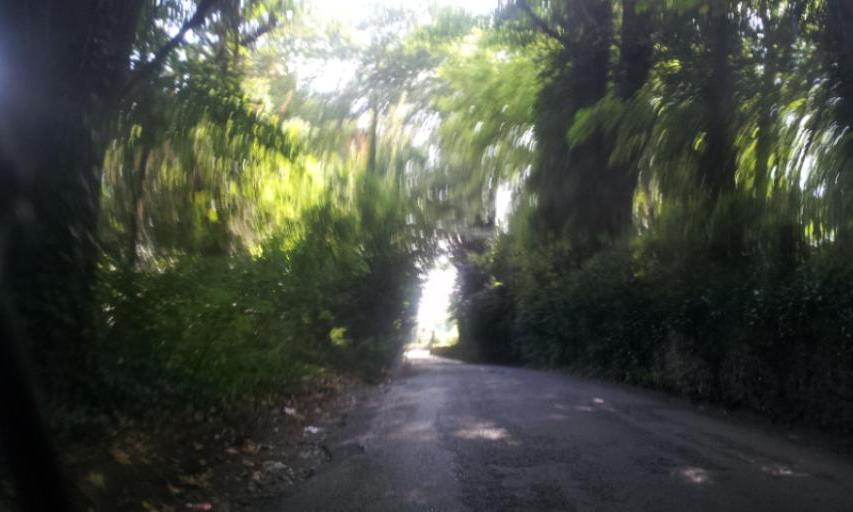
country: GB
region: England
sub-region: Kent
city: Maidstone
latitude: 51.2592
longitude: 0.5128
